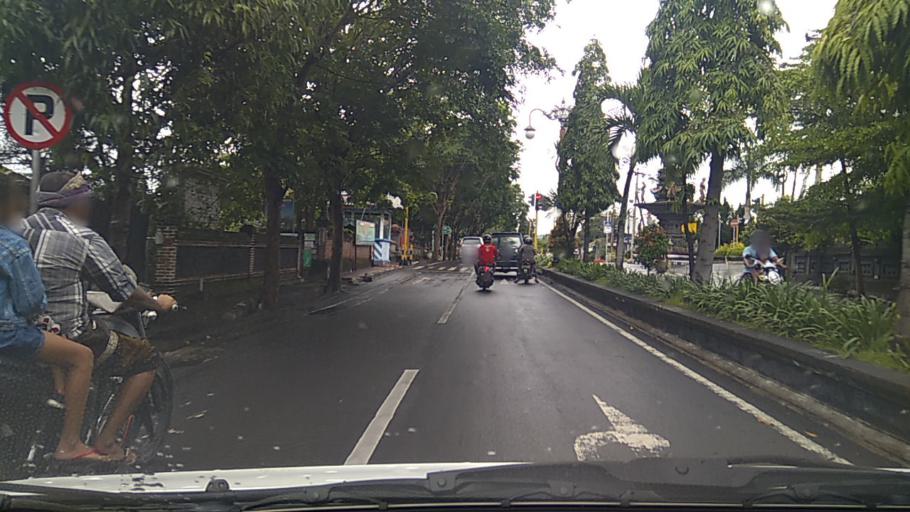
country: ID
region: Bali
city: Subagan
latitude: -8.4494
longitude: 115.6075
